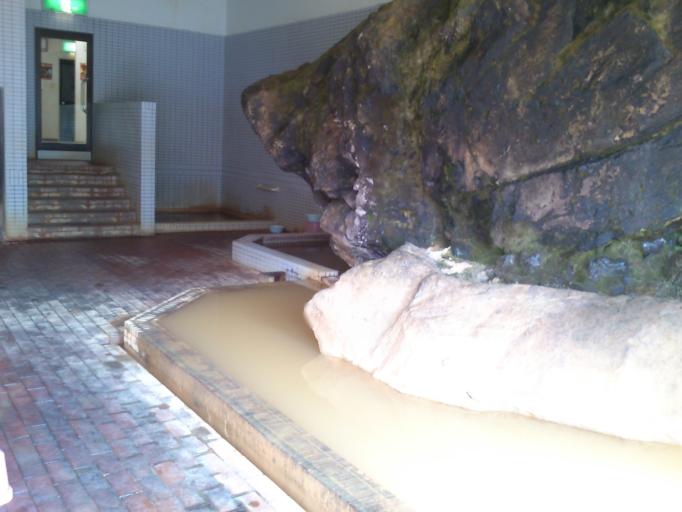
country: JP
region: Hokkaido
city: Shimo-furano
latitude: 43.4136
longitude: 142.6430
